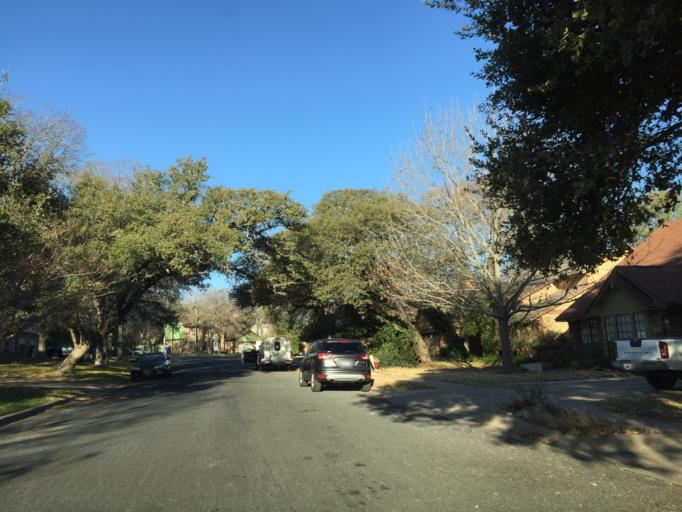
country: US
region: Texas
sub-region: Williamson County
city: Jollyville
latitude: 30.4411
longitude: -97.7663
